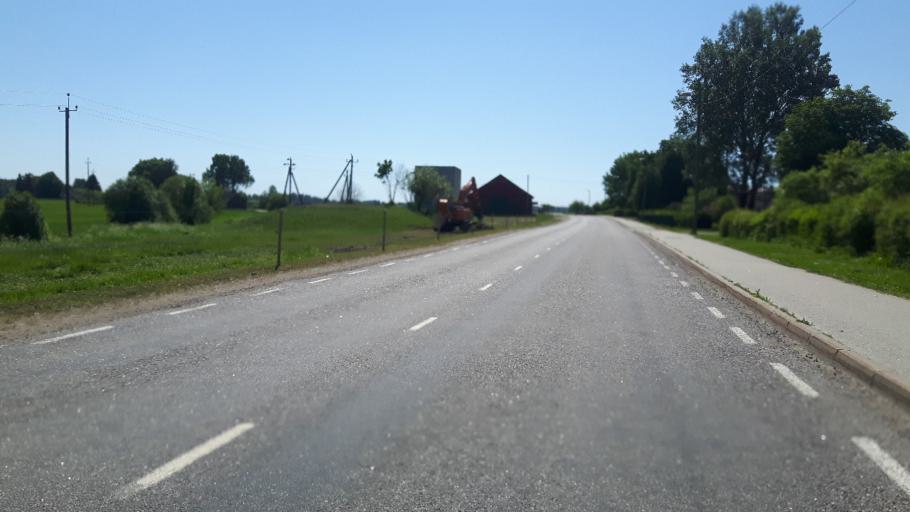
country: EE
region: Paernumaa
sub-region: Tootsi vald
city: Tootsi
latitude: 58.4795
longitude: 24.8084
